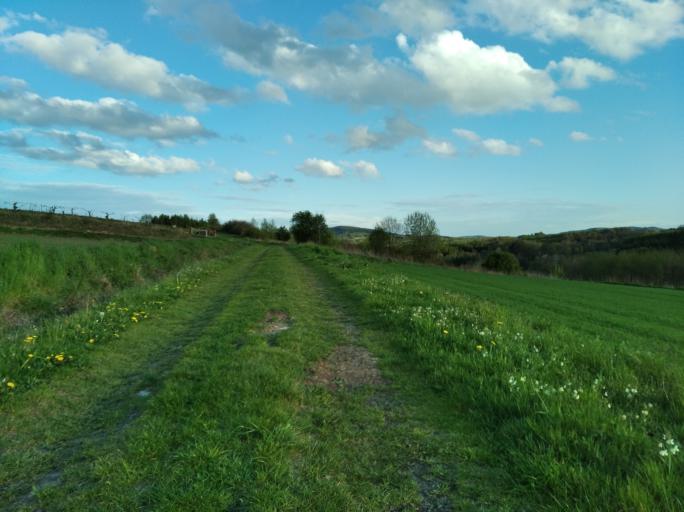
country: PL
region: Subcarpathian Voivodeship
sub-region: Powiat strzyzowski
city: Wysoka Strzyzowska
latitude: 49.8614
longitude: 21.7551
